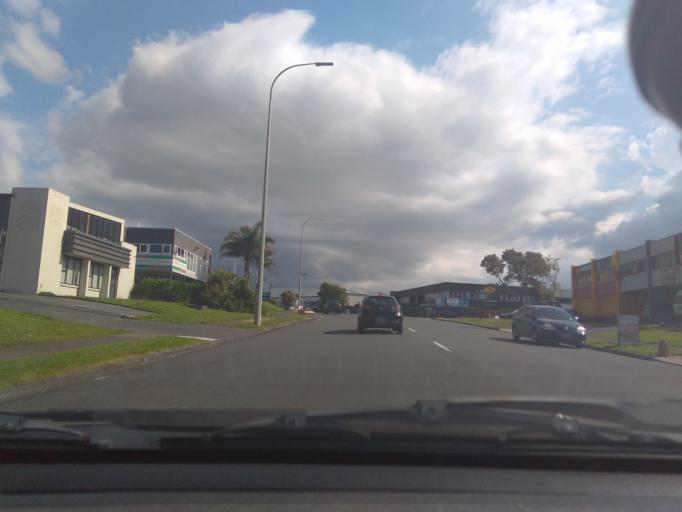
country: NZ
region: Auckland
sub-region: Auckland
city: Manukau City
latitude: -36.9445
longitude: 174.8816
